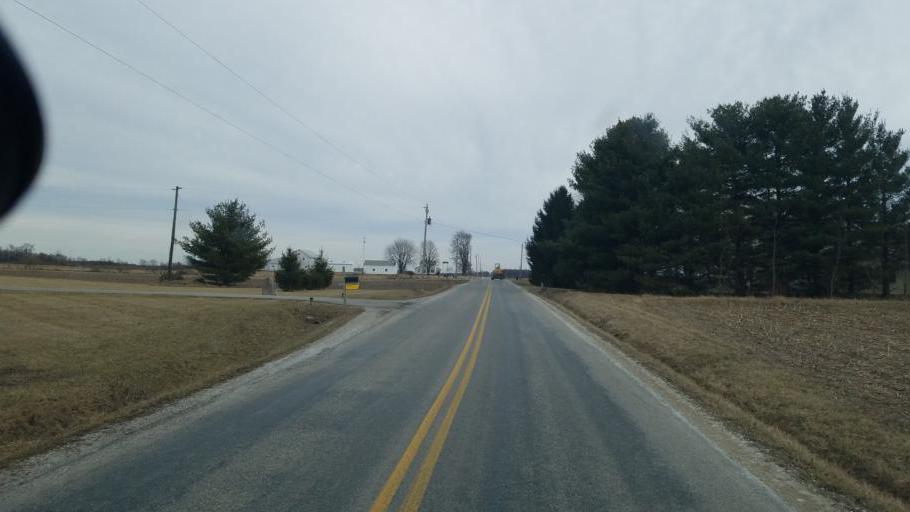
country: US
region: Ohio
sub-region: Marion County
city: Prospect
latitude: 40.4585
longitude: -83.0673
